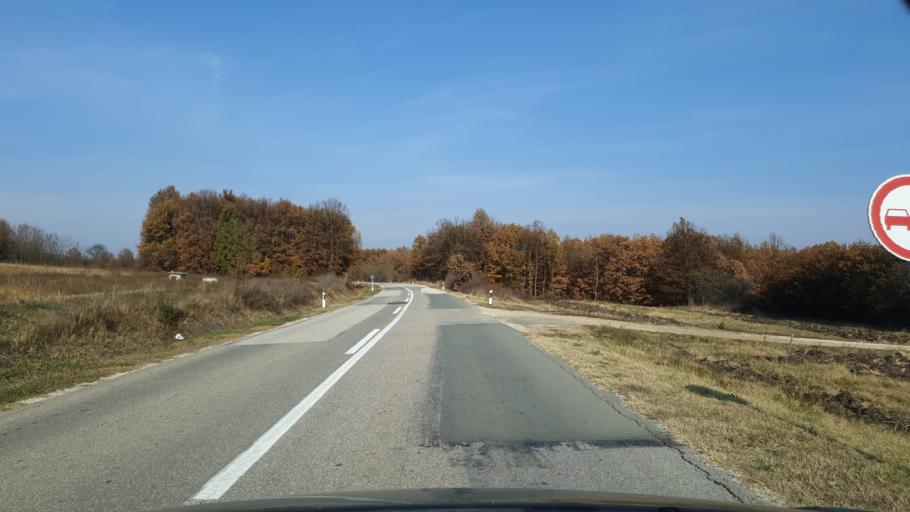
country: RS
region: Central Serbia
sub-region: Borski Okrug
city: Bor
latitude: 43.9507
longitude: 22.0928
